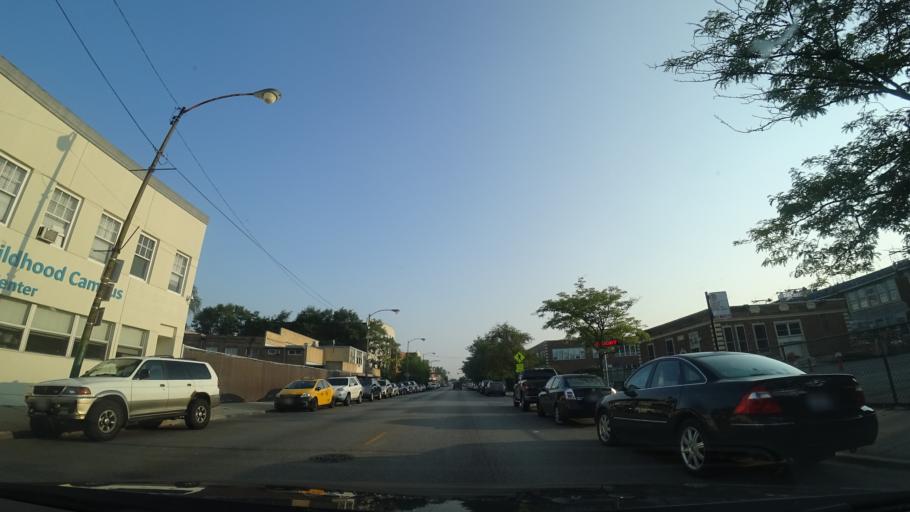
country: US
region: Illinois
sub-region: Cook County
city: Lincolnwood
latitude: 41.9925
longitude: -87.6995
